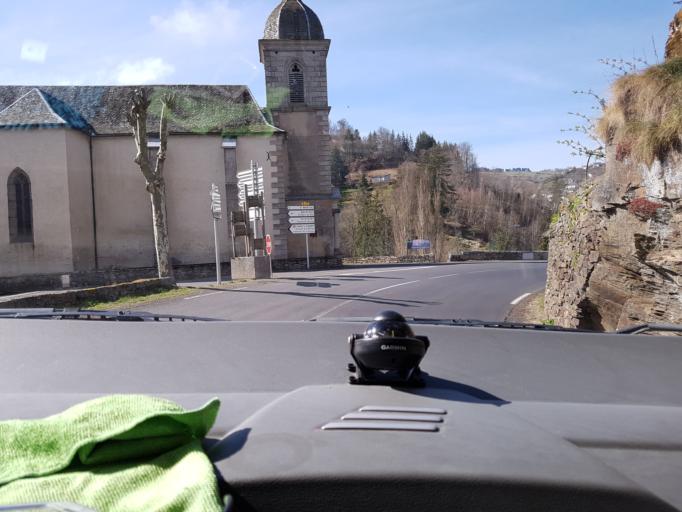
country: FR
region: Auvergne
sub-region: Departement du Cantal
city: Chaudes-Aigues
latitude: 44.8569
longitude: 3.0090
